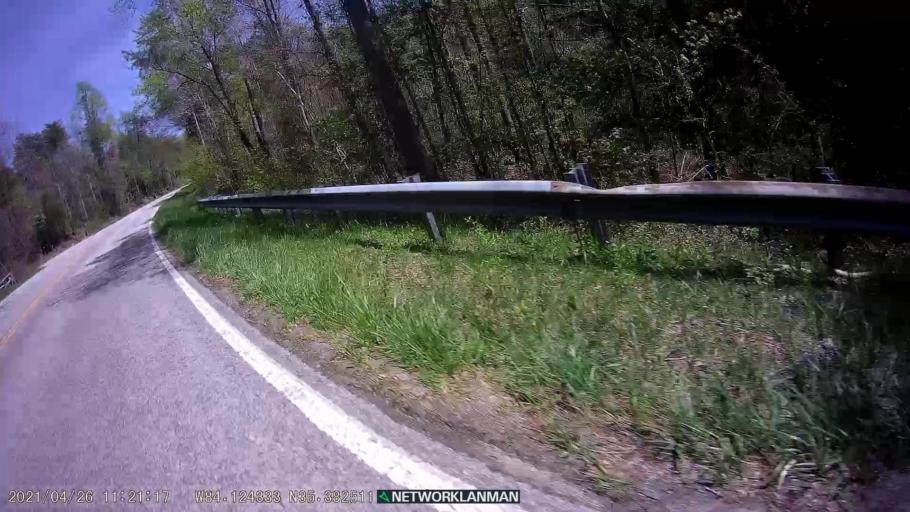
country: US
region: Tennessee
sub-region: Monroe County
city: Vonore
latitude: 35.3827
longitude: -84.1242
